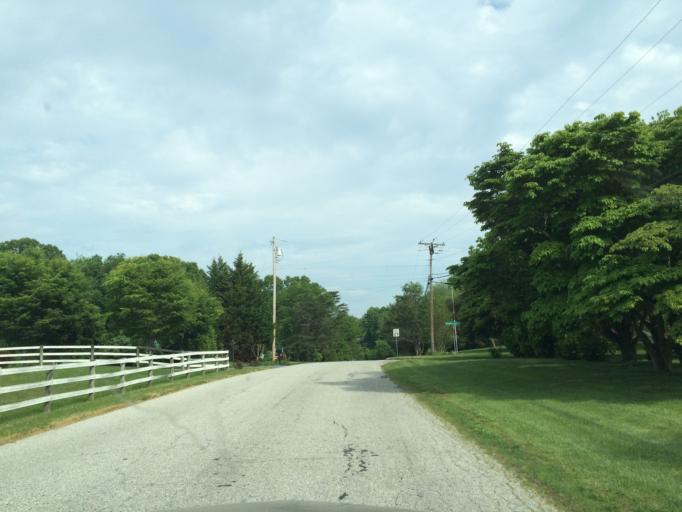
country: US
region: Maryland
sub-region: Baltimore County
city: Reisterstown
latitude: 39.4340
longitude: -76.8754
